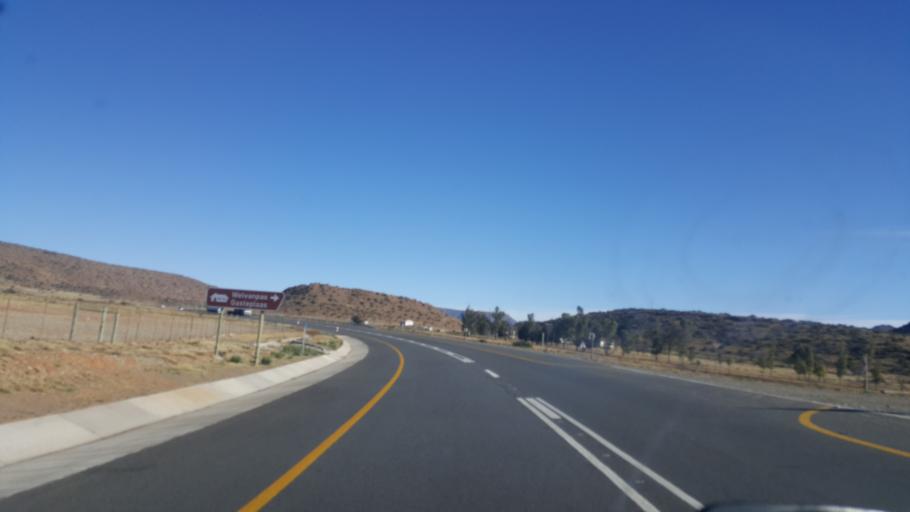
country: ZA
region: Eastern Cape
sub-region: Chris Hani District Municipality
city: Middelburg
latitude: -31.3762
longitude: 25.0332
